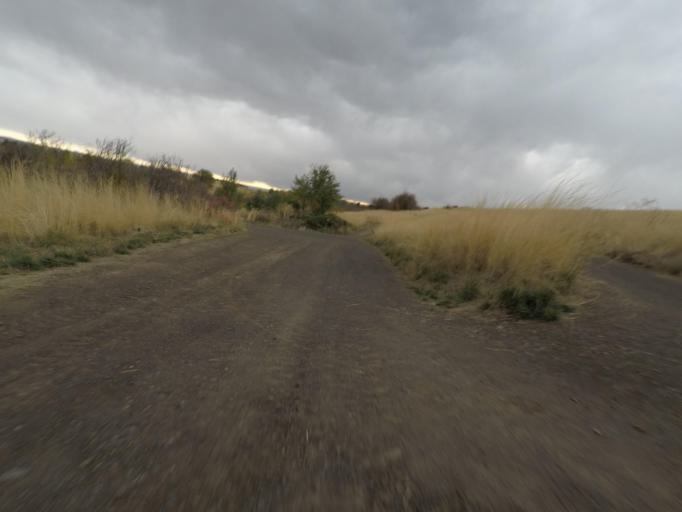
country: US
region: Washington
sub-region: Walla Walla County
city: Walla Walla East
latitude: 46.0760
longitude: -118.2577
